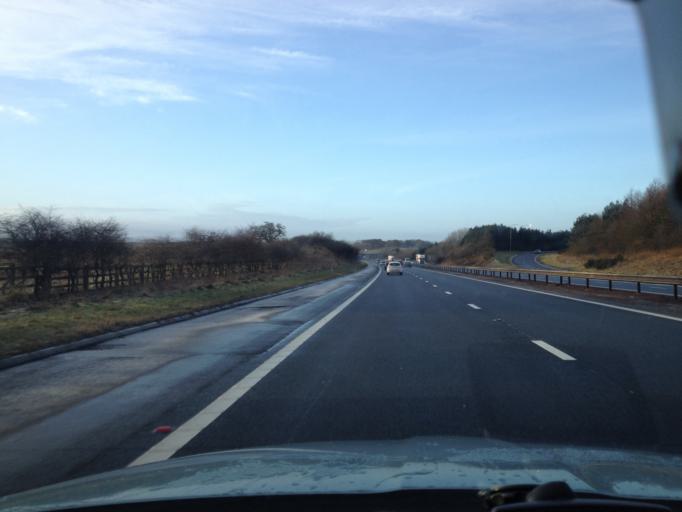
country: GB
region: Scotland
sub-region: West Lothian
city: West Calder
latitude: 55.8982
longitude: -3.5905
